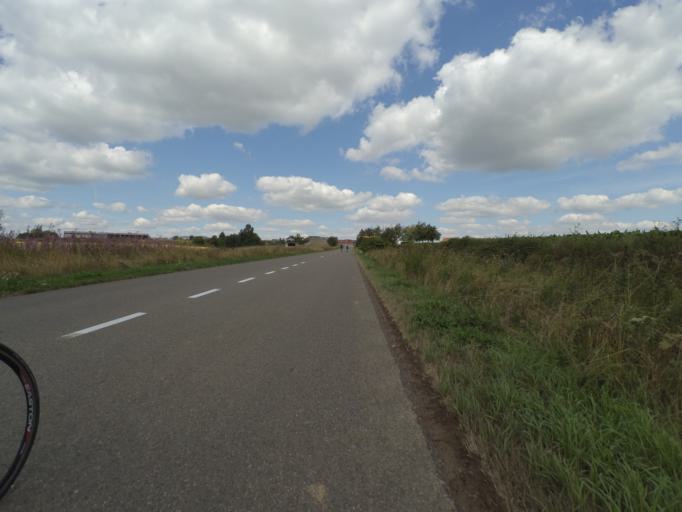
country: BE
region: Wallonia
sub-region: Province du Hainaut
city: Ellezelles
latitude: 50.7601
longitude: 3.6865
